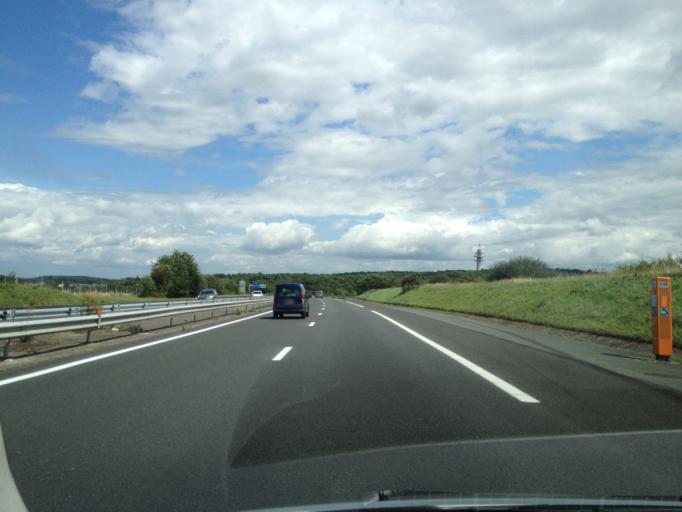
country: FR
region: Pays de la Loire
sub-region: Departement de la Sarthe
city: Rouillon
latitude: 48.0154
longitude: 0.1226
